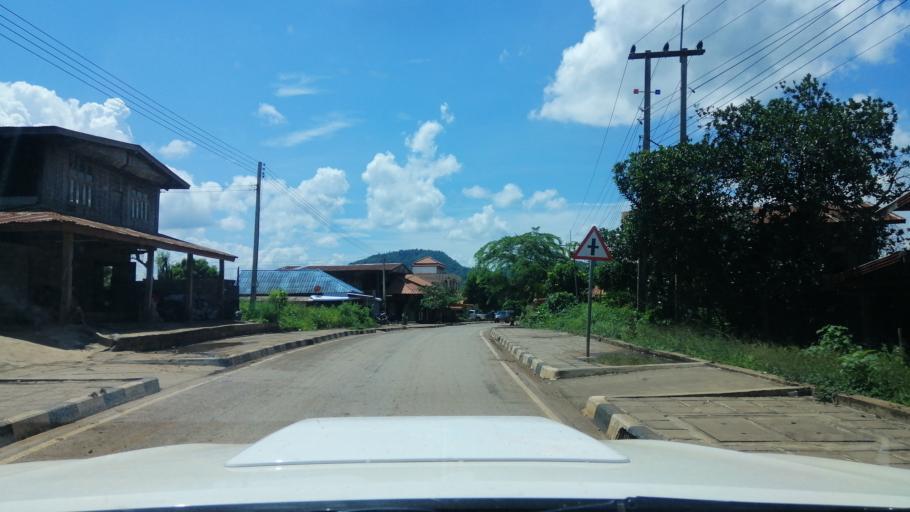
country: TH
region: Uttaradit
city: Ban Khok
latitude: 18.1360
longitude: 101.2707
